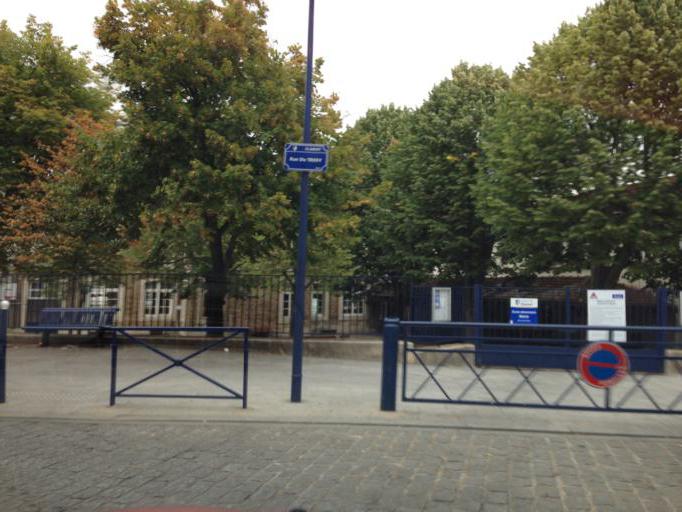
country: FR
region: Ile-de-France
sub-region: Departement des Hauts-de-Seine
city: Clamart
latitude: 48.8008
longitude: 2.2619
